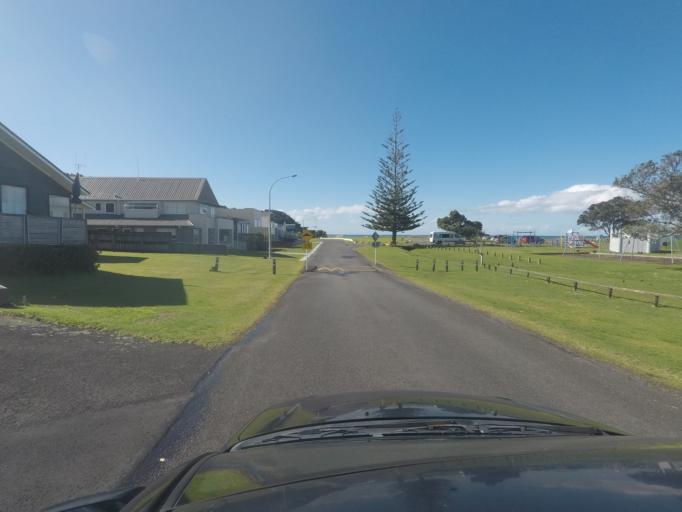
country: NZ
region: Bay of Plenty
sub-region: Western Bay of Plenty District
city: Waihi Beach
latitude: -37.4010
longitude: 175.9391
